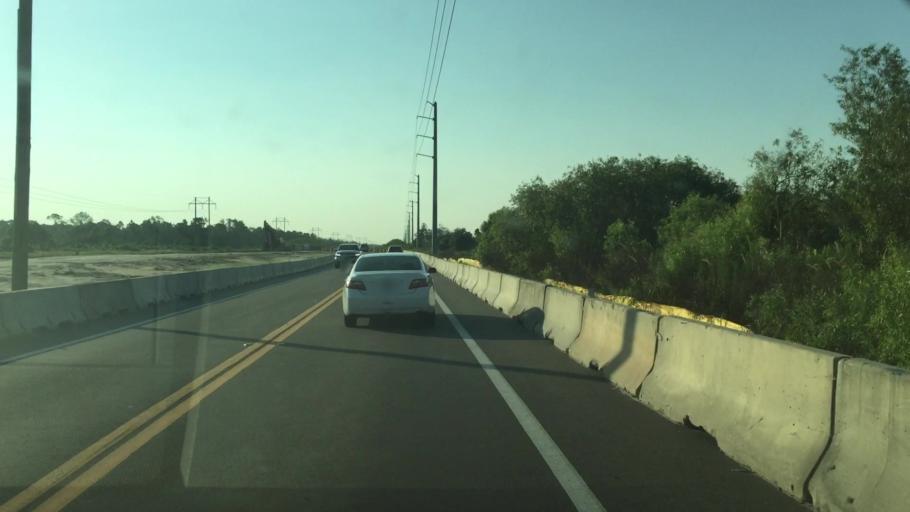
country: US
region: Florida
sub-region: Lee County
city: Gateway
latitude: 26.5770
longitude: -81.7033
